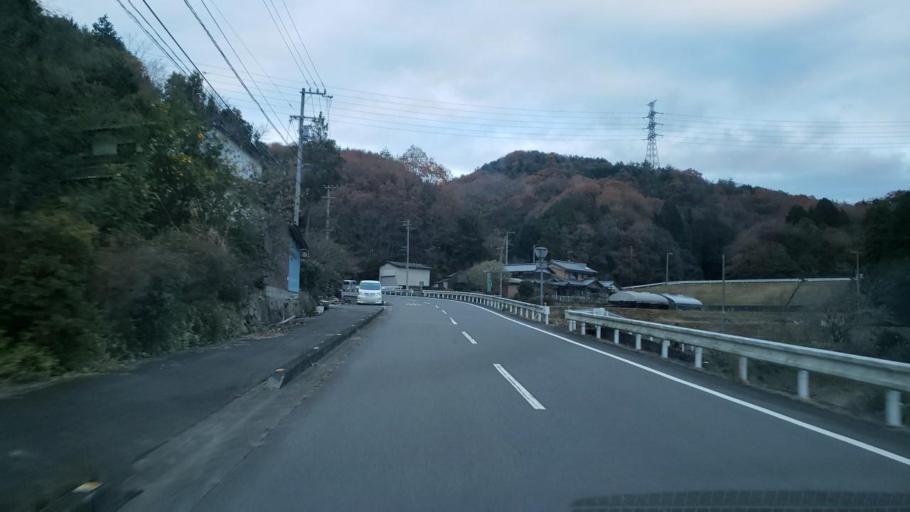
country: JP
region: Kagawa
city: Shido
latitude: 34.1939
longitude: 134.2502
